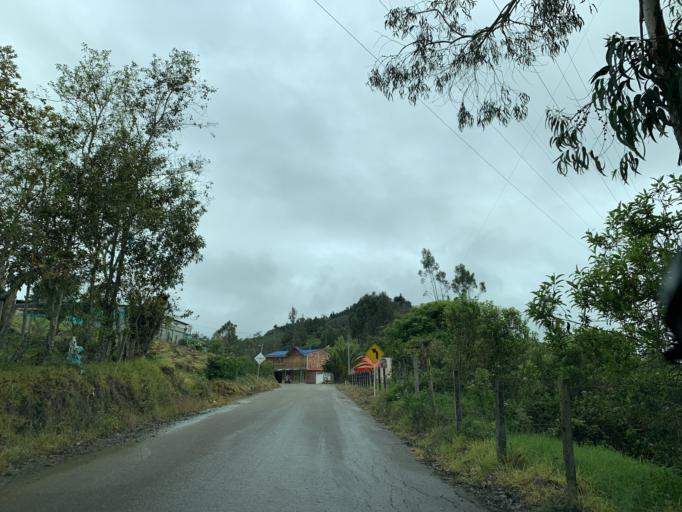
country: CO
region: Boyaca
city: Tibana
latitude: 5.3116
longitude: -73.4063
